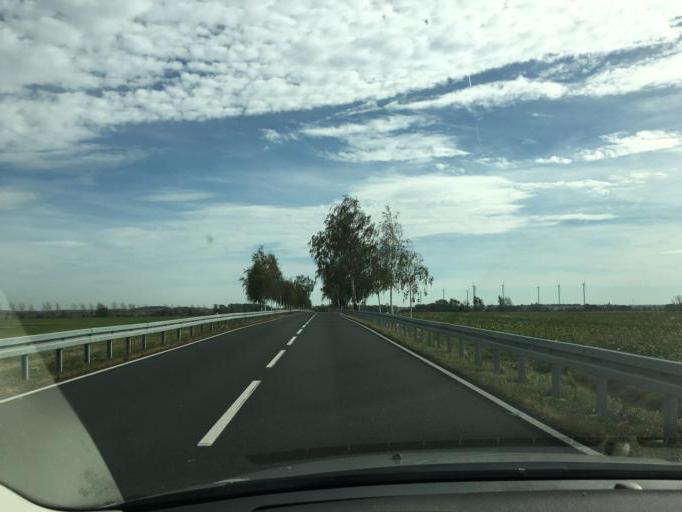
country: DE
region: Saxony
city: Lommatzsch
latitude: 51.2386
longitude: 13.3184
